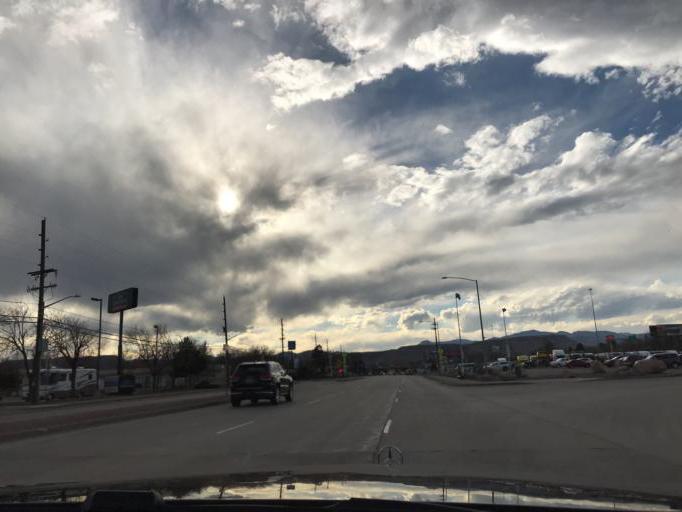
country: US
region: Colorado
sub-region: Jefferson County
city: Applewood
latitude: 39.7784
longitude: -105.1335
